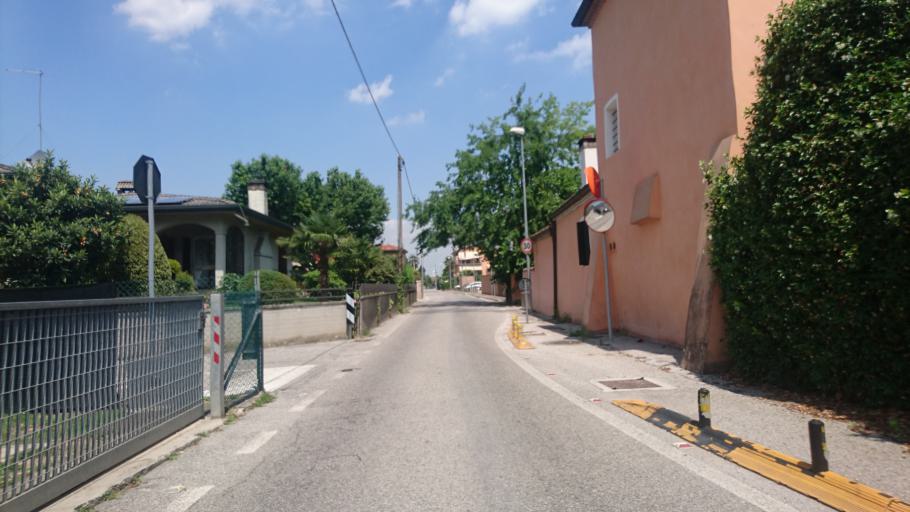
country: IT
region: Veneto
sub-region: Provincia di Venezia
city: Fiesso d'Artico
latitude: 45.4164
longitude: 12.0221
